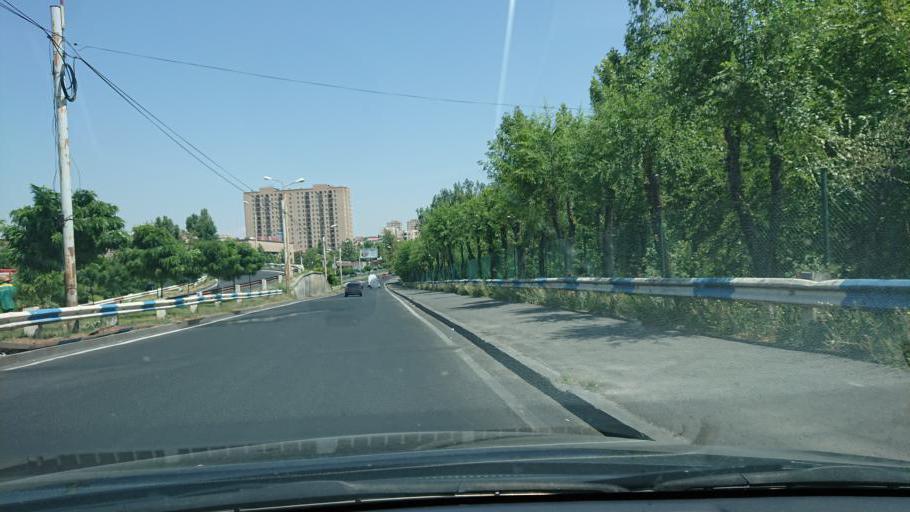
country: AM
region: Yerevan
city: Yerevan
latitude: 40.2127
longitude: 44.4919
